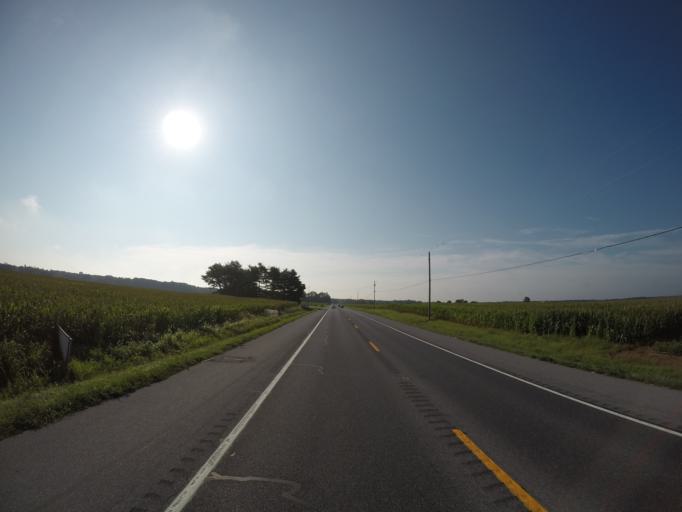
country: US
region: Delaware
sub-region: Sussex County
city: Bridgeville
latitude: 38.7136
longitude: -75.5717
